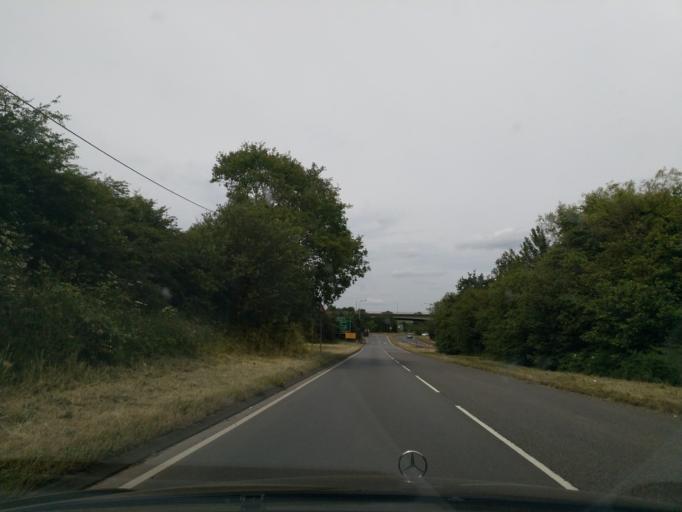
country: GB
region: England
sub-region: Solihull
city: Hampton in Arden
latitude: 52.4431
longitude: -1.6856
